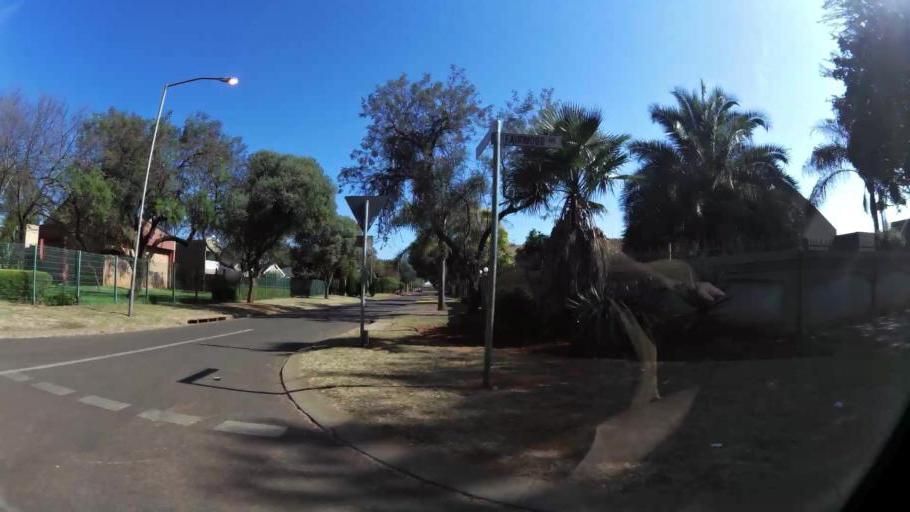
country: ZA
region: North-West
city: Ga-Rankuwa
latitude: -25.6468
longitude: 28.0981
